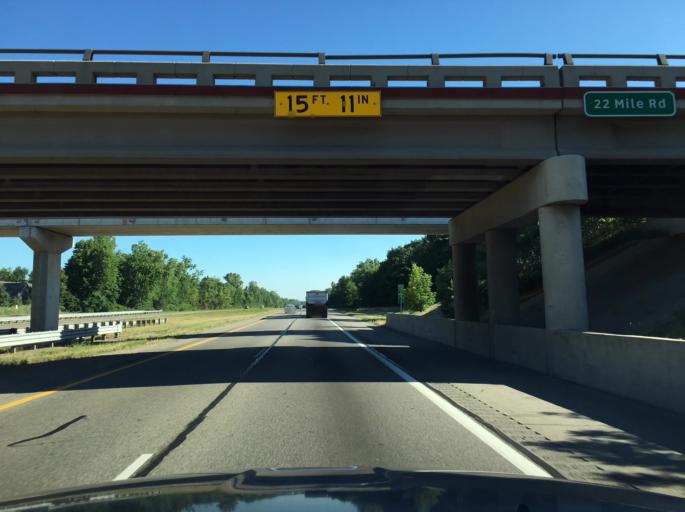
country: US
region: Michigan
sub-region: Macomb County
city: Shelby
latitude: 42.6551
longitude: -83.0141
